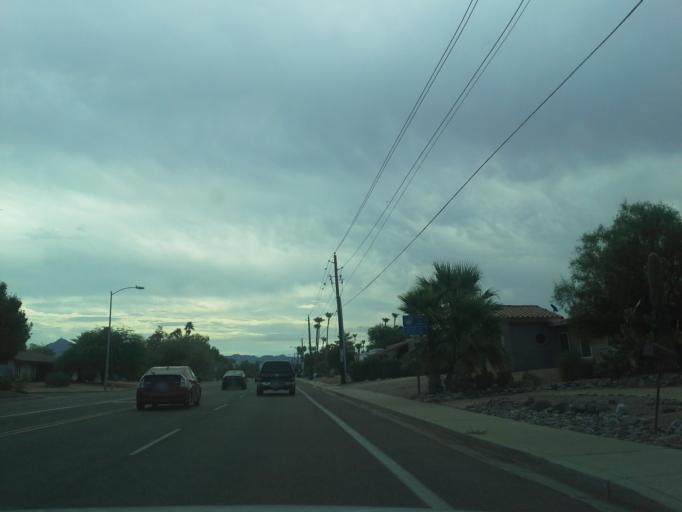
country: US
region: Arizona
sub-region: Maricopa County
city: Paradise Valley
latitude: 33.6113
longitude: -111.9428
